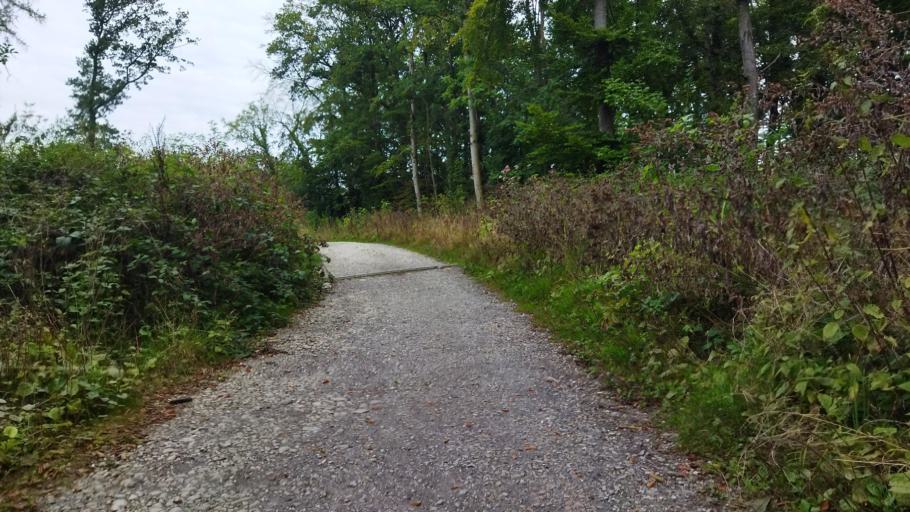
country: DE
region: Lower Saxony
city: Bad Rothenfelde
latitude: 52.1204
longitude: 8.1559
